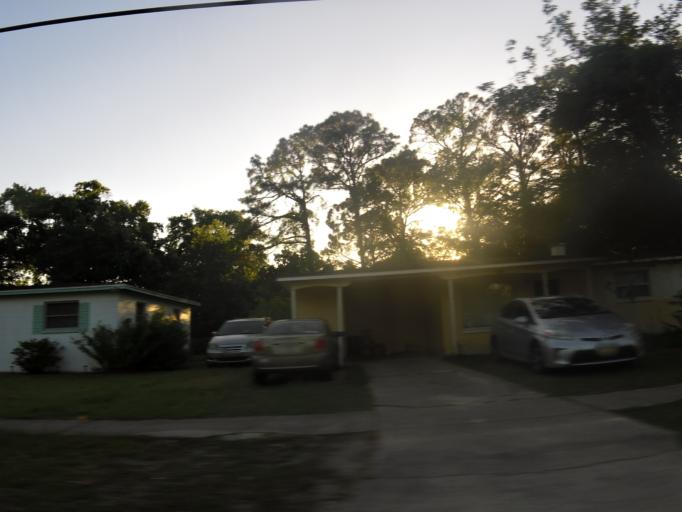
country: US
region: Florida
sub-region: Duval County
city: Jacksonville
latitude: 30.3474
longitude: -81.5688
